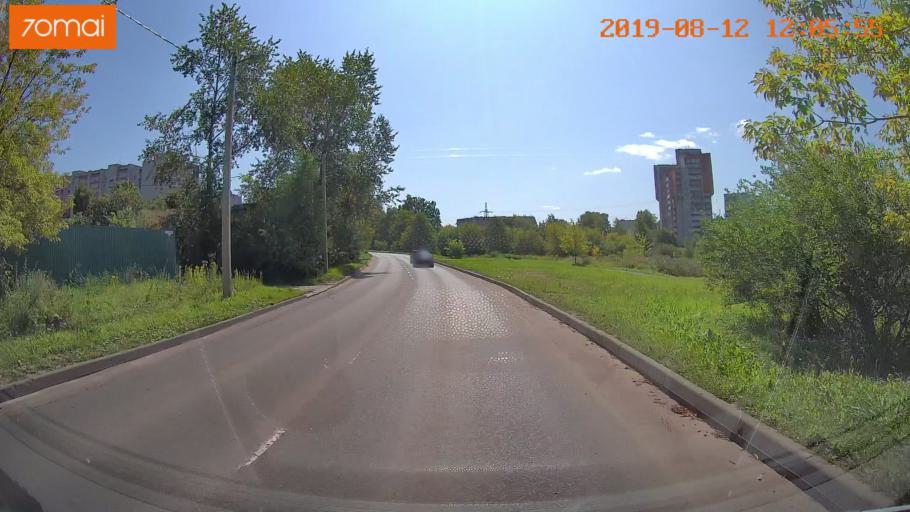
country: RU
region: Ivanovo
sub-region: Gorod Ivanovo
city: Ivanovo
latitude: 56.9912
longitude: 41.0189
